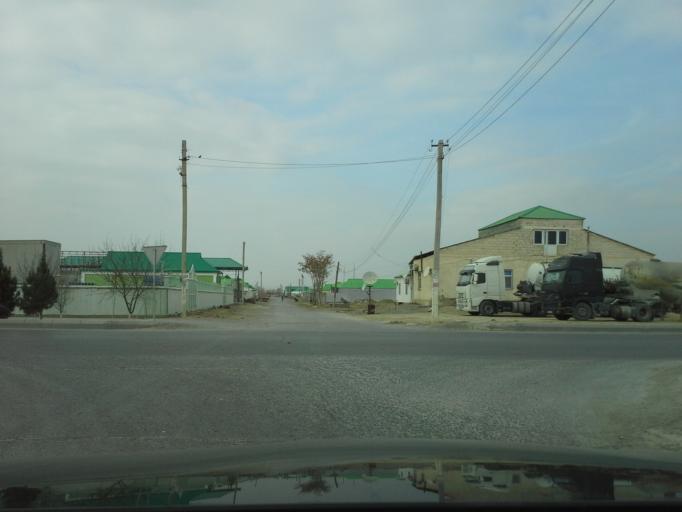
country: TM
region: Ahal
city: Abadan
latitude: 38.0316
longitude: 58.2493
